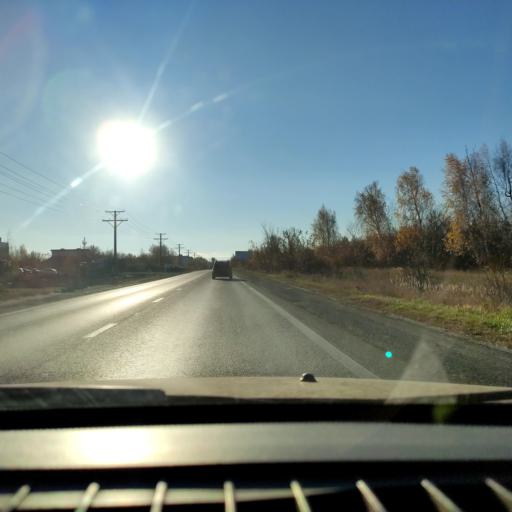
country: RU
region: Samara
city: Tol'yatti
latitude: 53.5573
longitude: 49.3629
